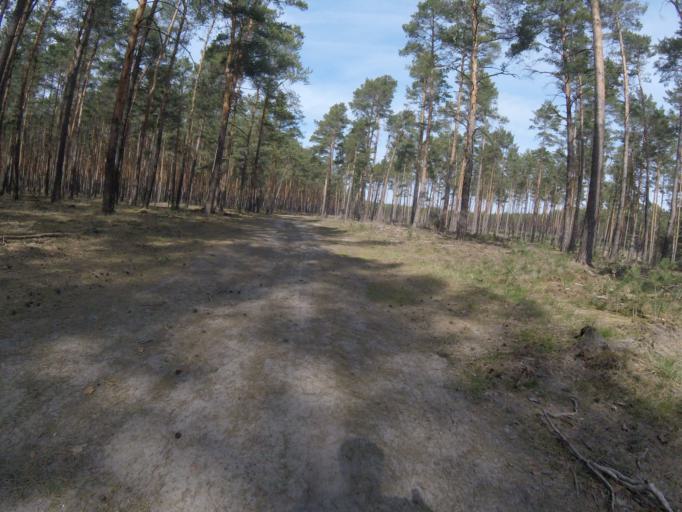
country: DE
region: Brandenburg
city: Gross Koris
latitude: 52.2046
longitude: 13.6645
